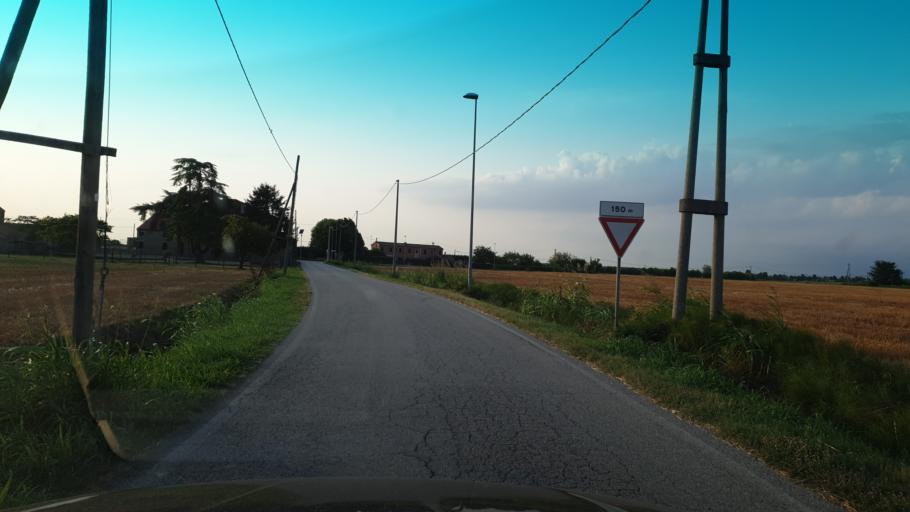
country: IT
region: Veneto
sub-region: Provincia di Rovigo
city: Castelguglielmo
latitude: 45.0098
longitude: 11.5261
